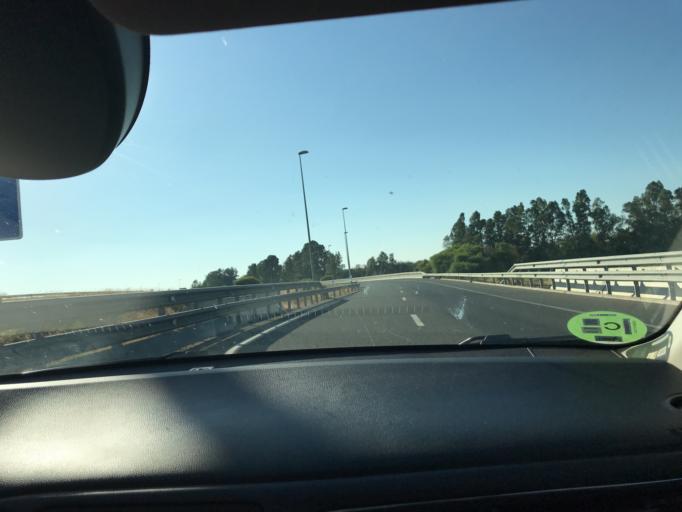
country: ES
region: Andalusia
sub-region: Provincia de Sevilla
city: Alcala de Guadaira
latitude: 37.4323
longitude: -5.8383
